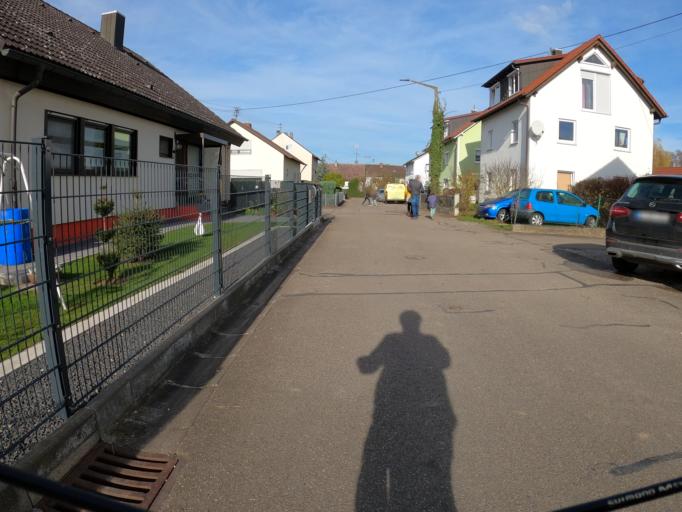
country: DE
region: Bavaria
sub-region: Swabia
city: Leipheim
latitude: 48.4005
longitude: 10.1997
